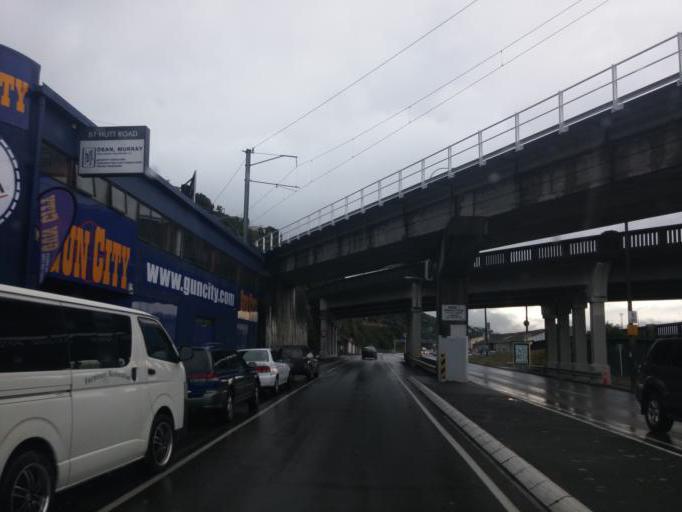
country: NZ
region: Wellington
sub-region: Wellington City
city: Wellington
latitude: -41.2646
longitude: 174.7842
